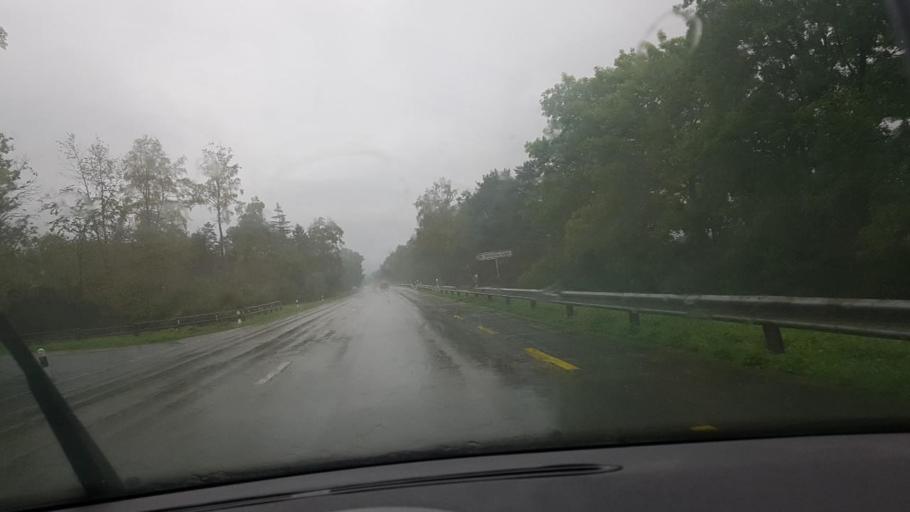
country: LI
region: Triesen
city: Triesen
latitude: 47.0866
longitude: 9.5187
